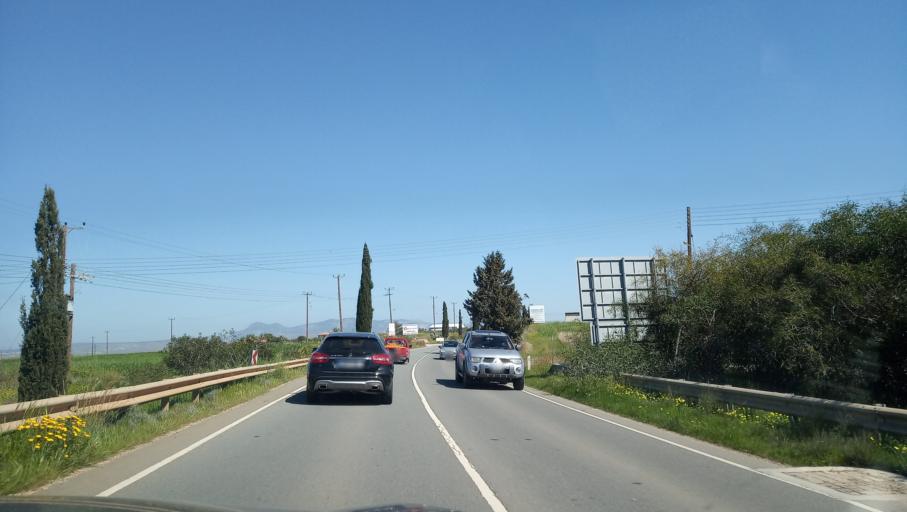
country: CY
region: Lefkosia
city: Astromeritis
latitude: 35.1305
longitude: 33.0151
